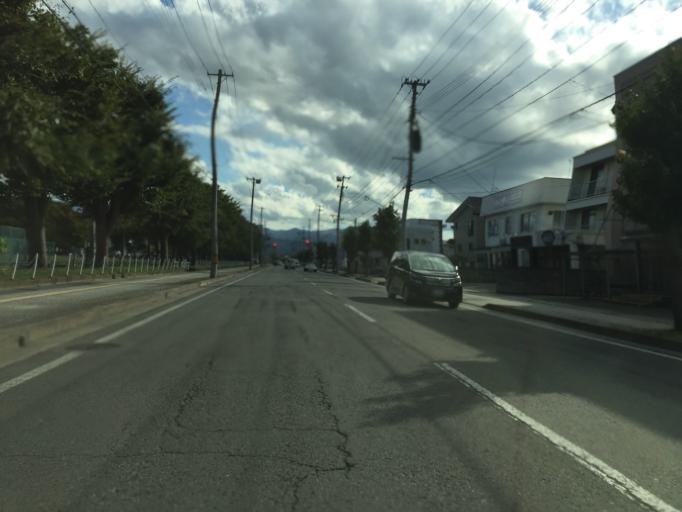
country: JP
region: Yamagata
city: Yonezawa
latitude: 37.9192
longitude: 140.1174
